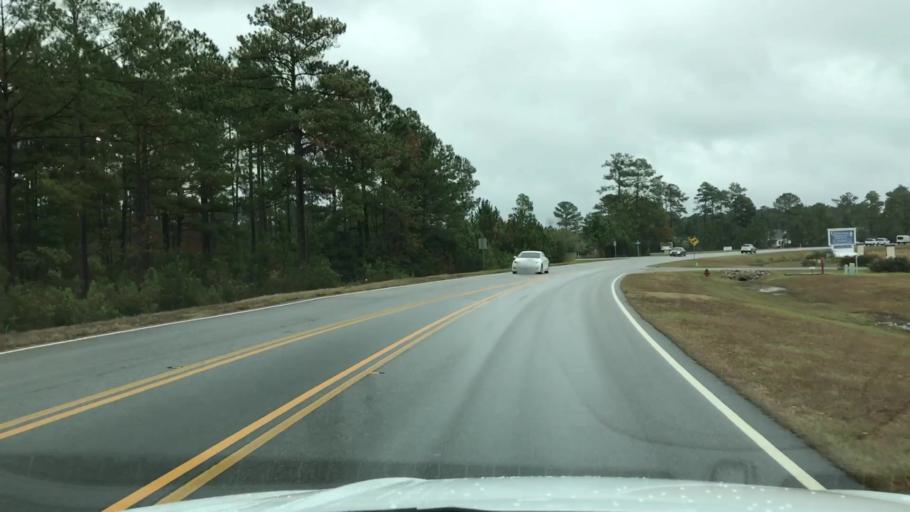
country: US
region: South Carolina
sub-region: Horry County
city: Myrtle Beach
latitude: 33.7615
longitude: -78.8879
